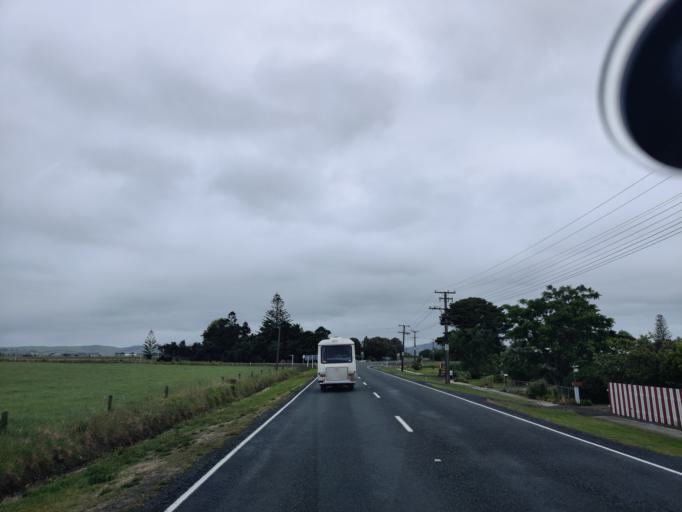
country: NZ
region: Northland
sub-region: Kaipara District
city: Dargaville
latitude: -36.1294
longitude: 174.0348
